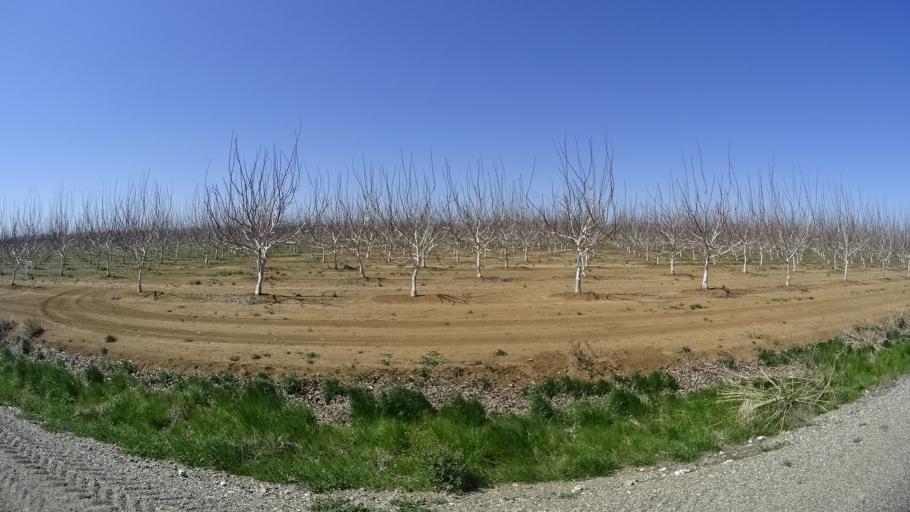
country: US
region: California
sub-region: Glenn County
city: Willows
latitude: 39.4403
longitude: -122.2487
